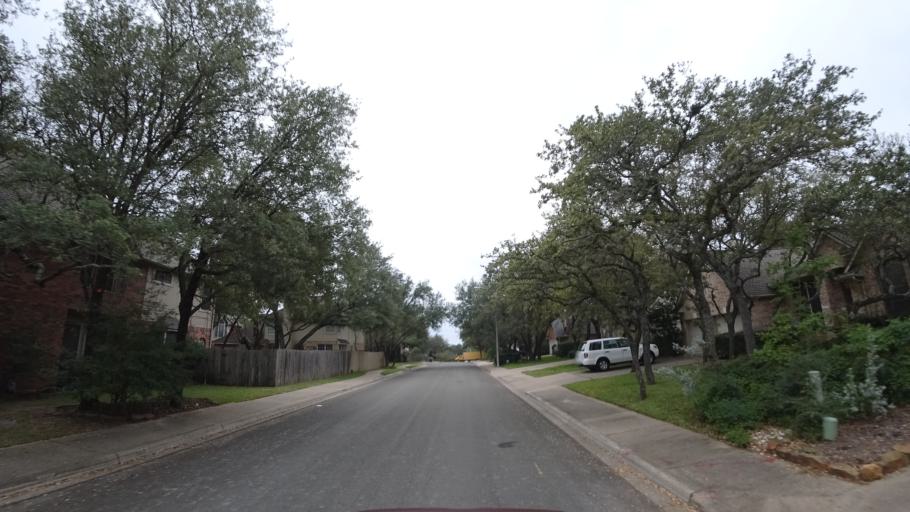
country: US
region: Texas
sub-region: Williamson County
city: Anderson Mill
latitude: 30.4379
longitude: -97.8290
